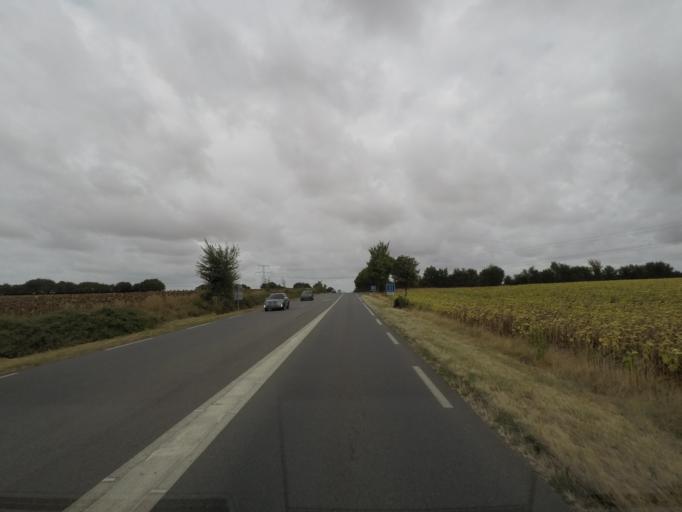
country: FR
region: Poitou-Charentes
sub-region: Departement des Deux-Sevres
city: Thorigne
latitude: 46.2741
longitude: -0.2389
